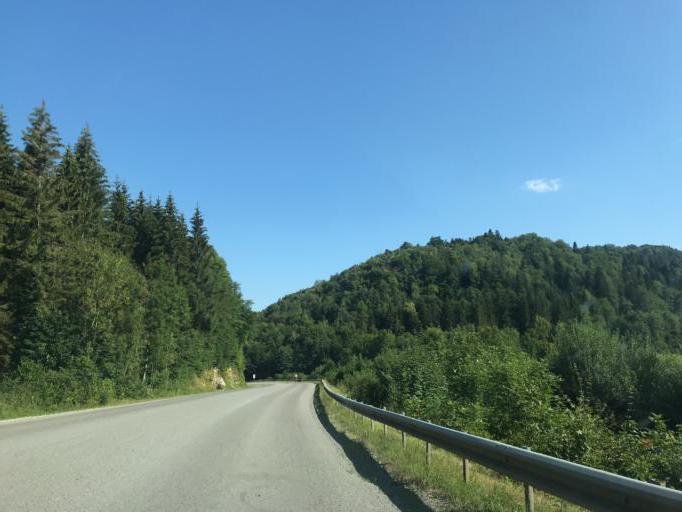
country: FR
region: Franche-Comte
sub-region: Departement du Jura
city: Lavans-les-Saint-Claude
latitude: 46.3925
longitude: 5.7395
